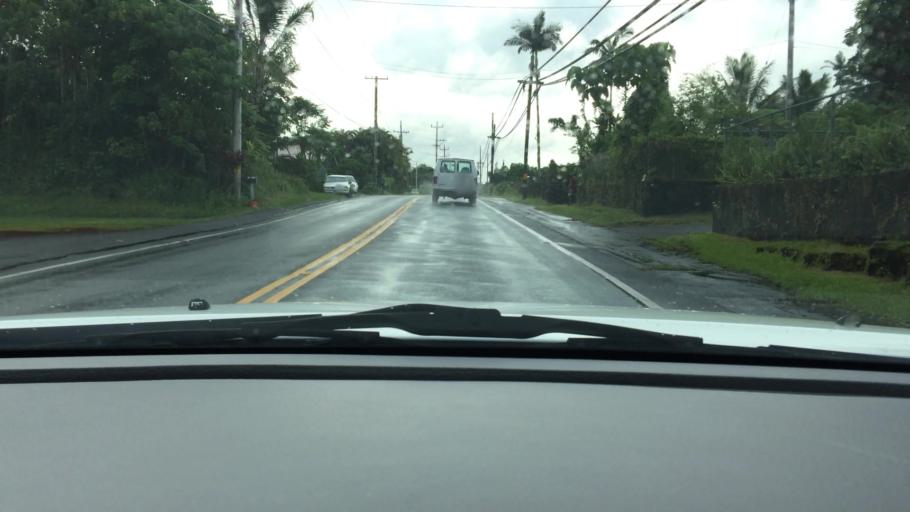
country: US
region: Hawaii
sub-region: Hawaii County
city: Hawaiian Paradise Park
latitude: 19.4963
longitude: -154.9507
